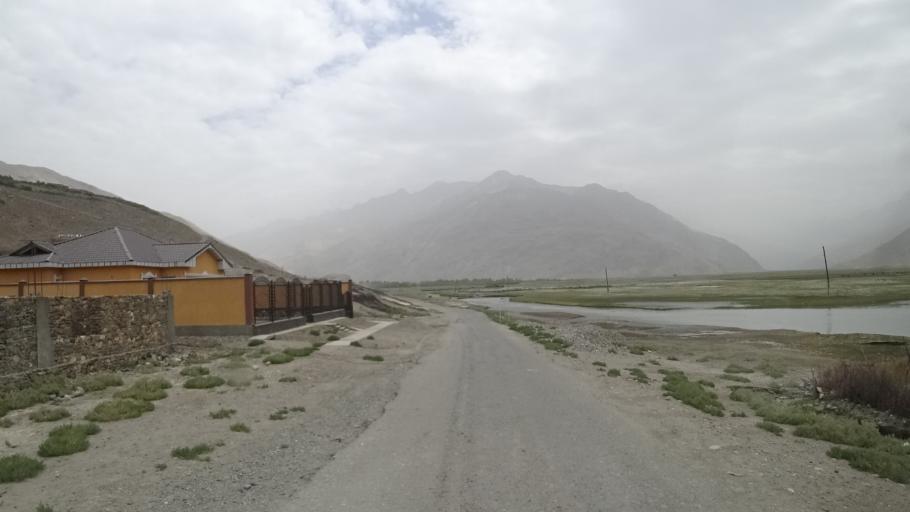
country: AF
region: Badakhshan
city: Khandud
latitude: 37.0321
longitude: 72.6321
